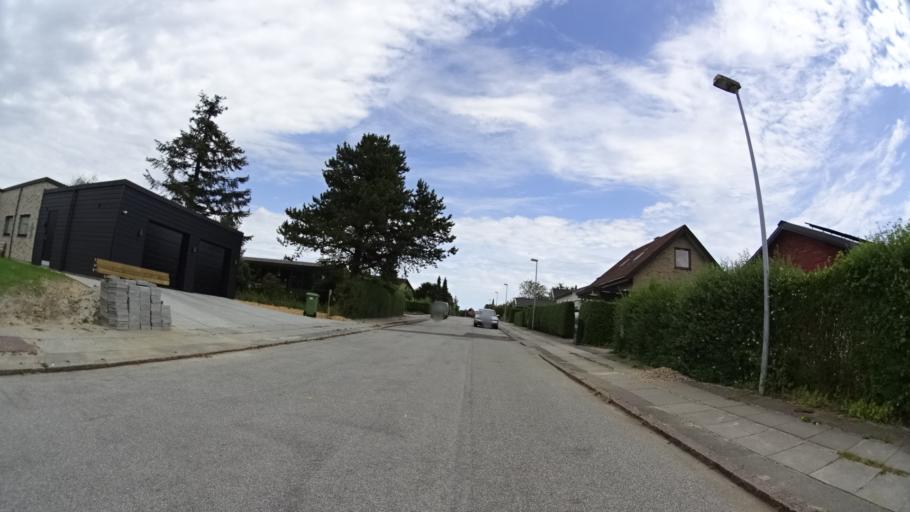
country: DK
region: Central Jutland
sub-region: Arhus Kommune
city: Stavtrup
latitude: 56.1273
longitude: 10.1463
